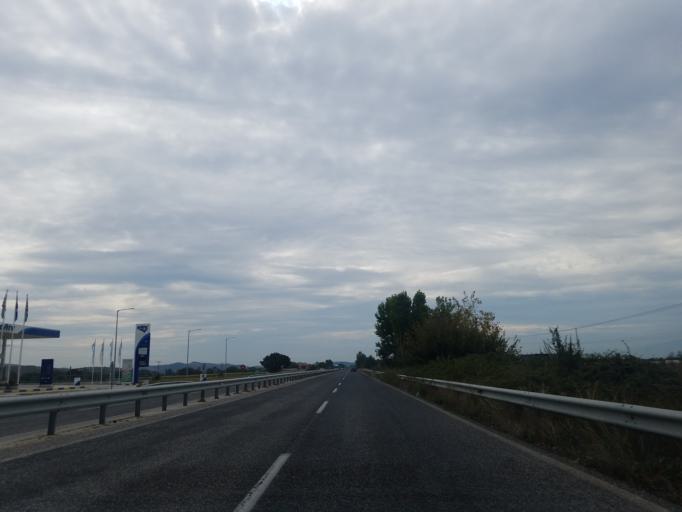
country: GR
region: Thessaly
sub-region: Trikala
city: Vasiliki
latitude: 39.6179
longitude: 21.7153
